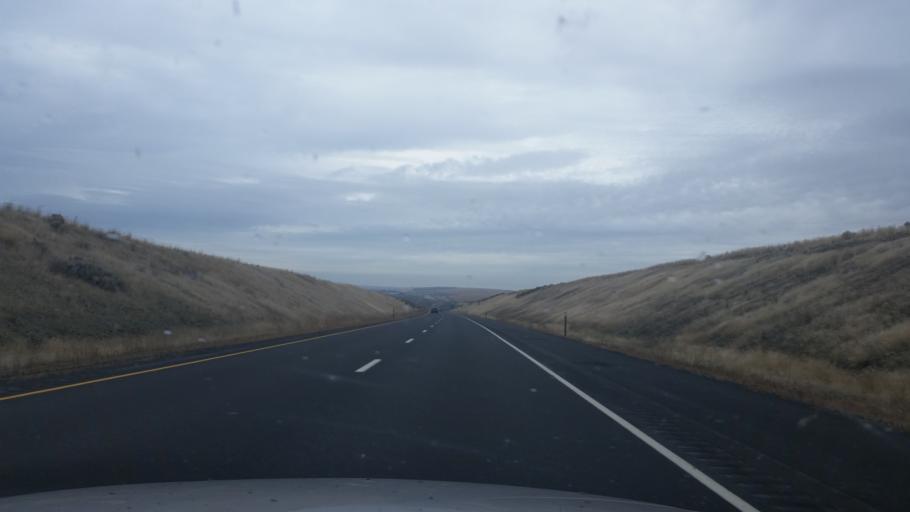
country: US
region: Washington
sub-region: Grant County
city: Warden
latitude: 47.0871
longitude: -118.8600
